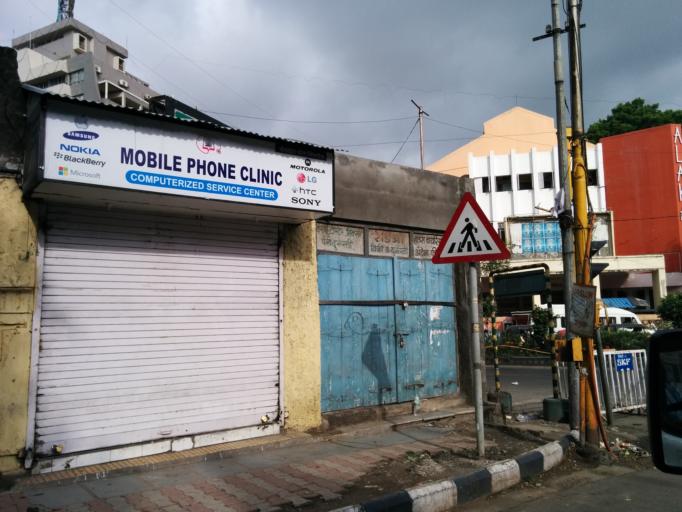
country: IN
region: Maharashtra
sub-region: Pune Division
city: Pune
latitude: 18.5119
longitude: 73.8440
